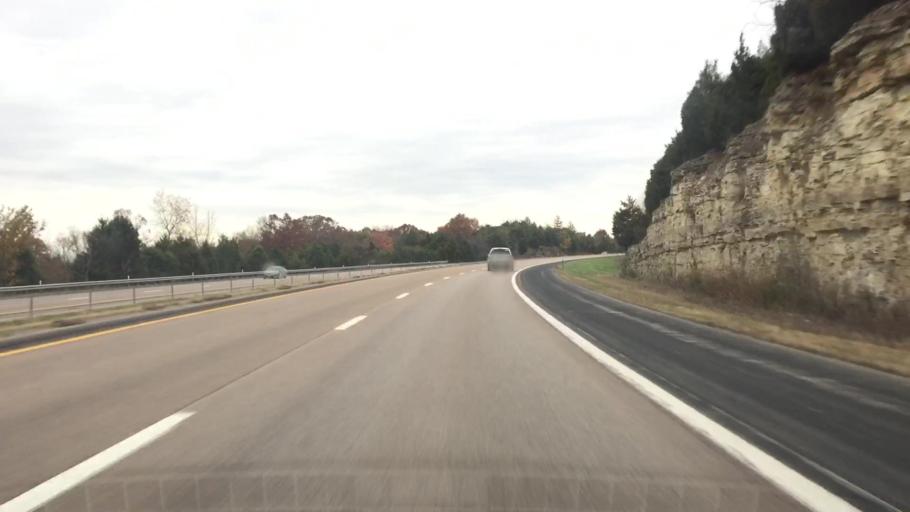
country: US
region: Missouri
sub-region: Boone County
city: Ashland
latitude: 38.6788
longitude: -92.2508
